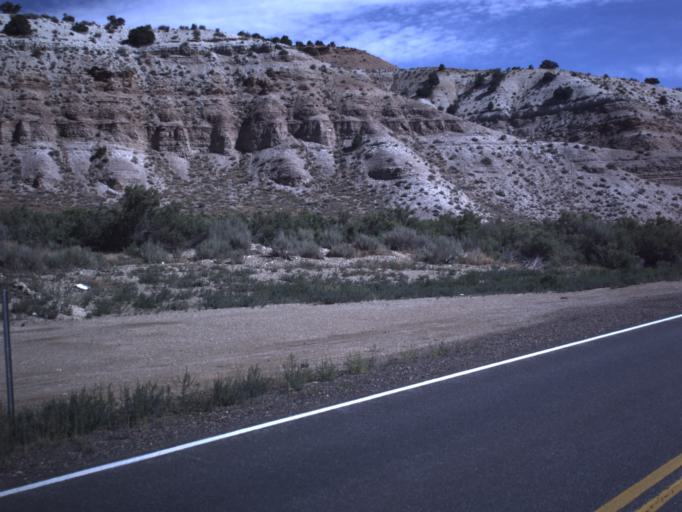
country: US
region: Utah
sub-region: Duchesne County
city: Duchesne
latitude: 40.1138
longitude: -110.4548
